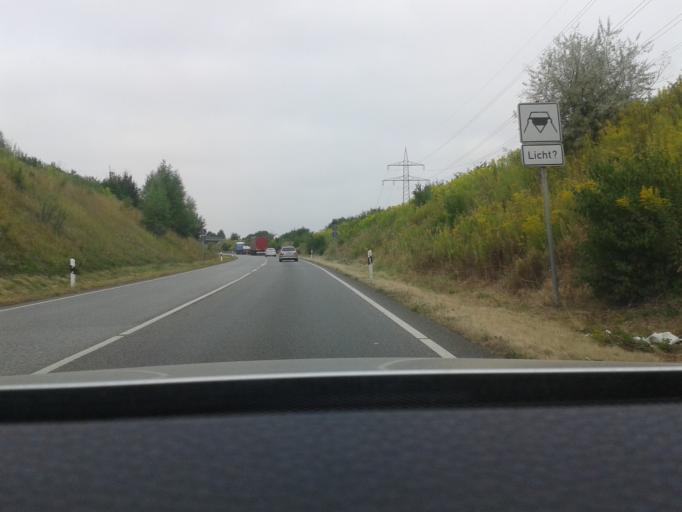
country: DE
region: Saxony
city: Kreischa
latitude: 50.9951
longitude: 13.7793
